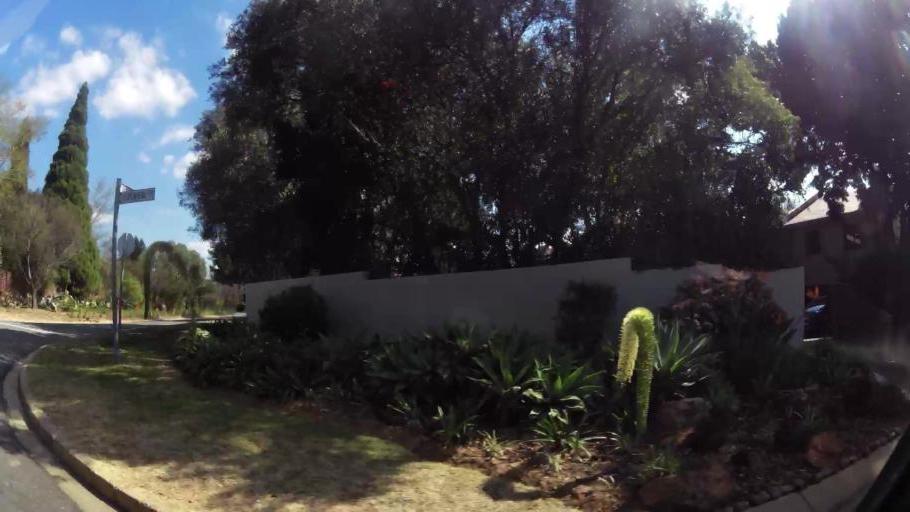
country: ZA
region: Gauteng
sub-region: City of Johannesburg Metropolitan Municipality
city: Roodepoort
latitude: -26.0855
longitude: 27.9537
